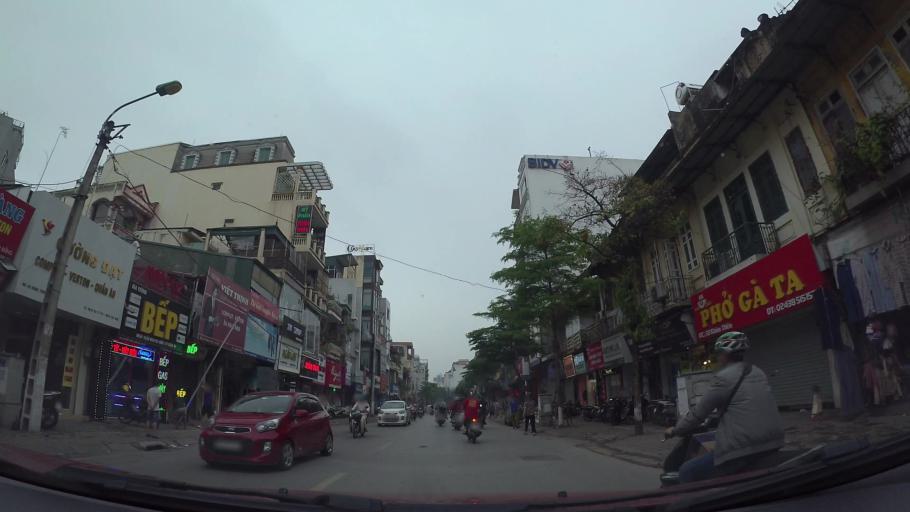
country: VN
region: Ha Noi
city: Hanoi
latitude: 21.0190
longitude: 105.8388
